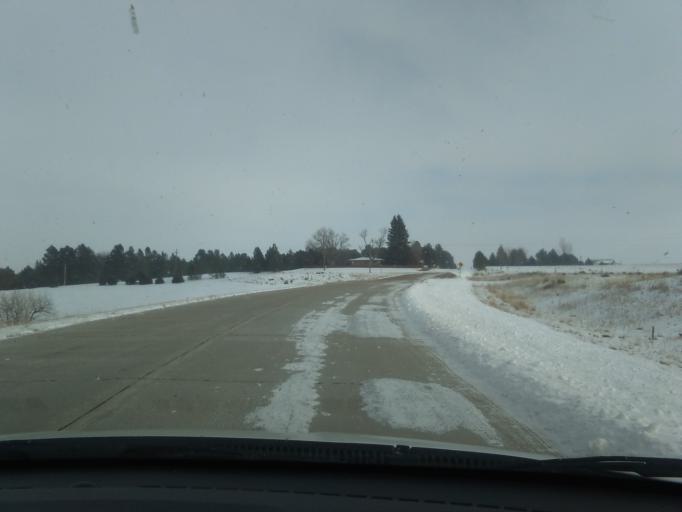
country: US
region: Nebraska
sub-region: Kimball County
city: Kimball
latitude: 41.2242
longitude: -103.6269
